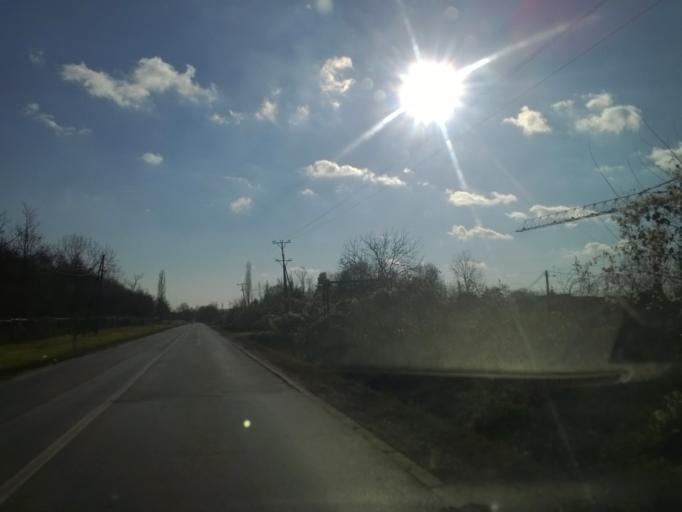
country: RS
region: Central Serbia
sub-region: Podunavski Okrug
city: Smederevo
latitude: 44.6016
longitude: 20.9633
